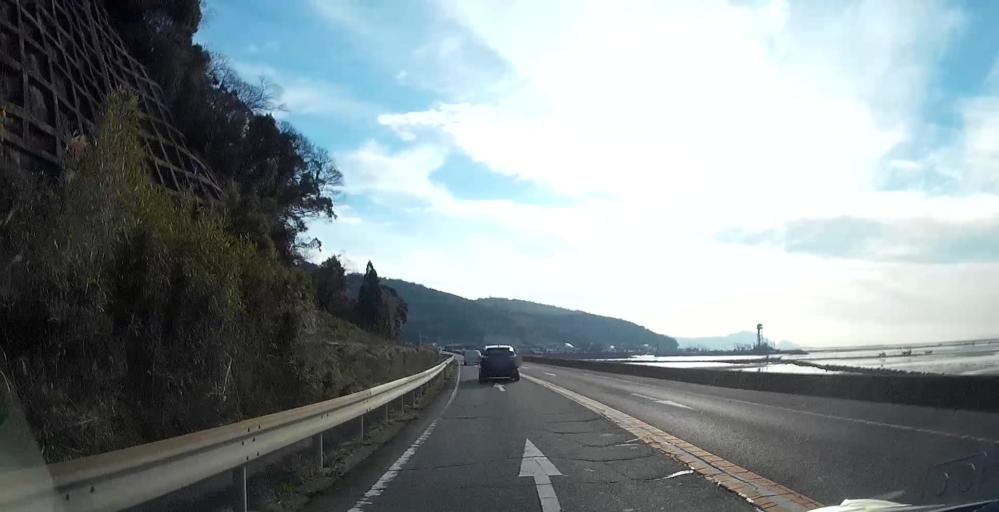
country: JP
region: Kumamoto
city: Uto
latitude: 32.6980
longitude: 130.5668
